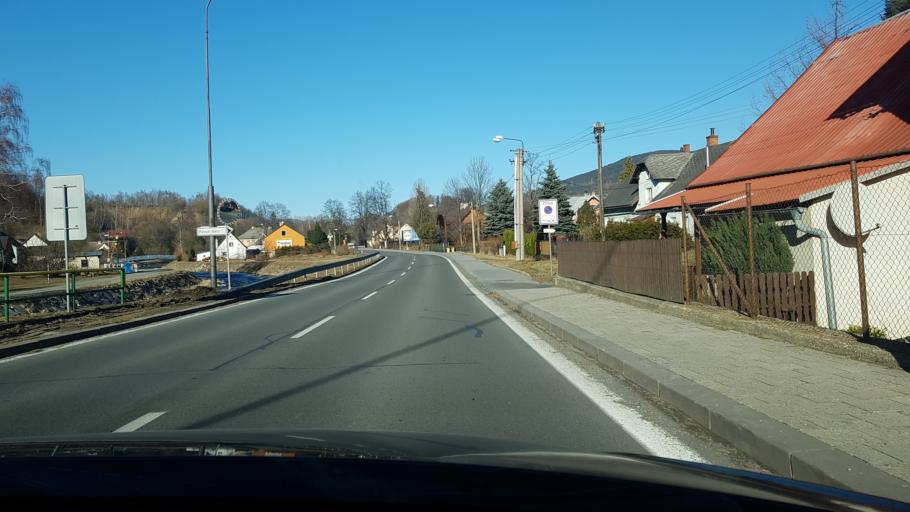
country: CZ
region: Olomoucky
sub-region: Okres Jesenik
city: Jesenik
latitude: 50.2073
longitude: 17.1965
